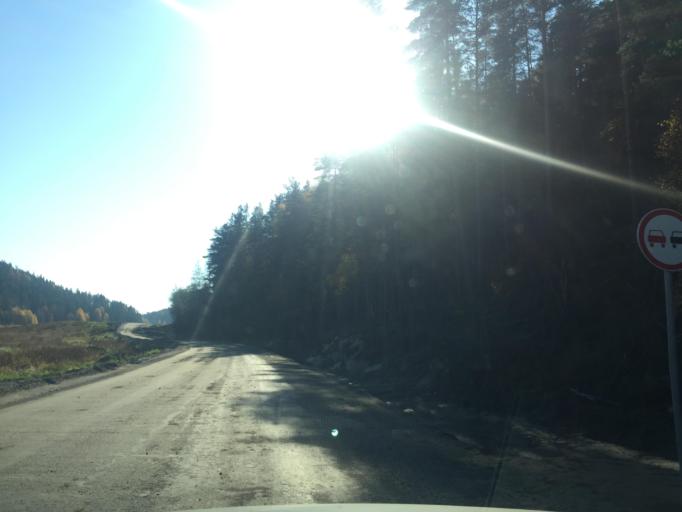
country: RU
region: Leningrad
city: Kuznechnoye
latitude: 61.3240
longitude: 29.8654
